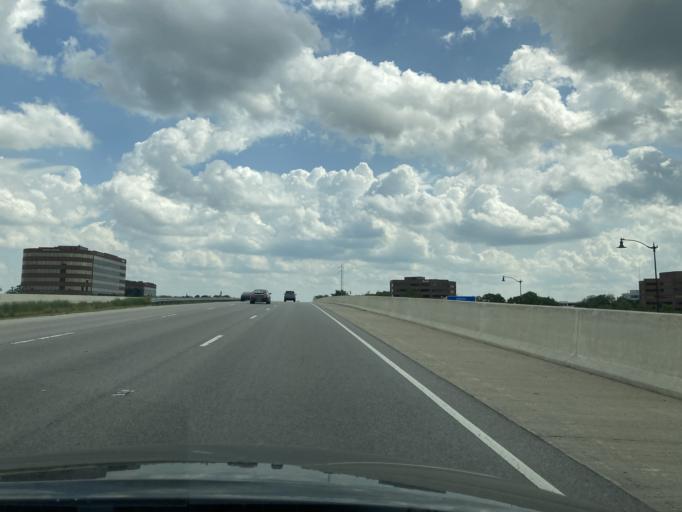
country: US
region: Indiana
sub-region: Hamilton County
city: Carmel
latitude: 39.9579
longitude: -86.1580
